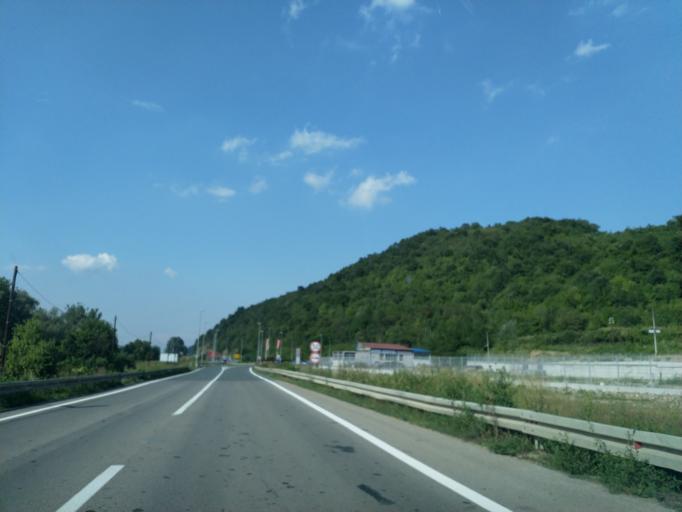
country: RS
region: Central Serbia
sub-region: Rasinski Okrug
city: Krusevac
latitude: 43.6257
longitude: 21.3747
